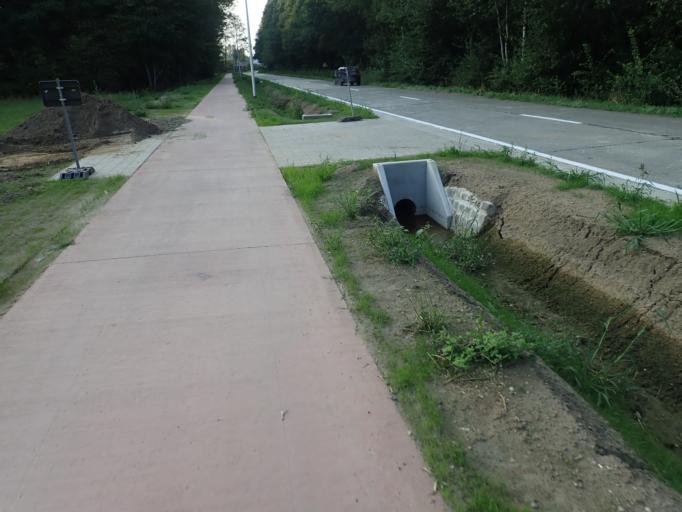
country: BE
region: Flanders
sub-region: Provincie Antwerpen
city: Berlaar
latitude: 51.1315
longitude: 4.6408
